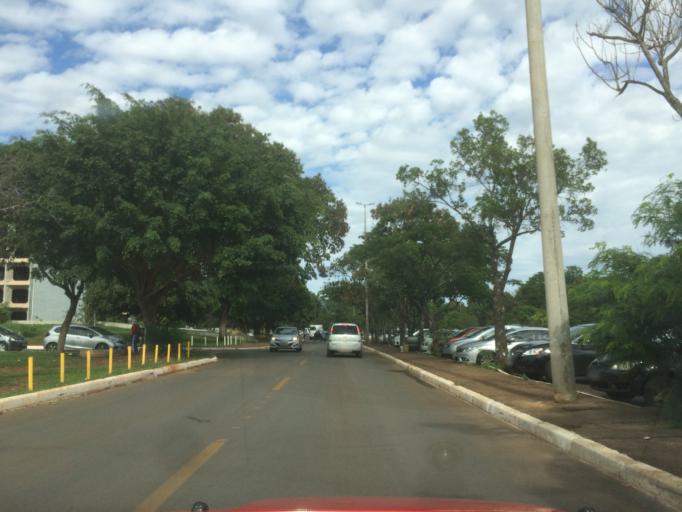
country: BR
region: Federal District
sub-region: Brasilia
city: Brasilia
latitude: -15.7939
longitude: -47.8680
